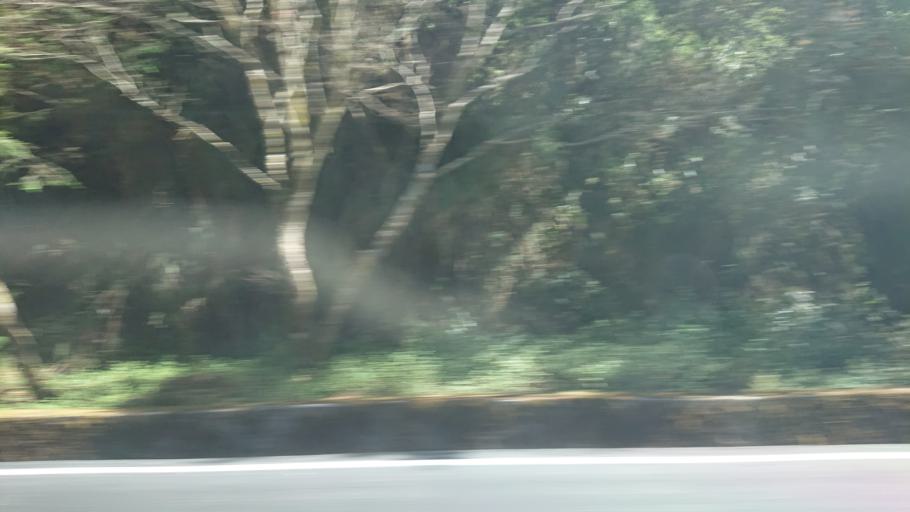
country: TW
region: Taiwan
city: Lugu
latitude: 23.4977
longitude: 120.8184
